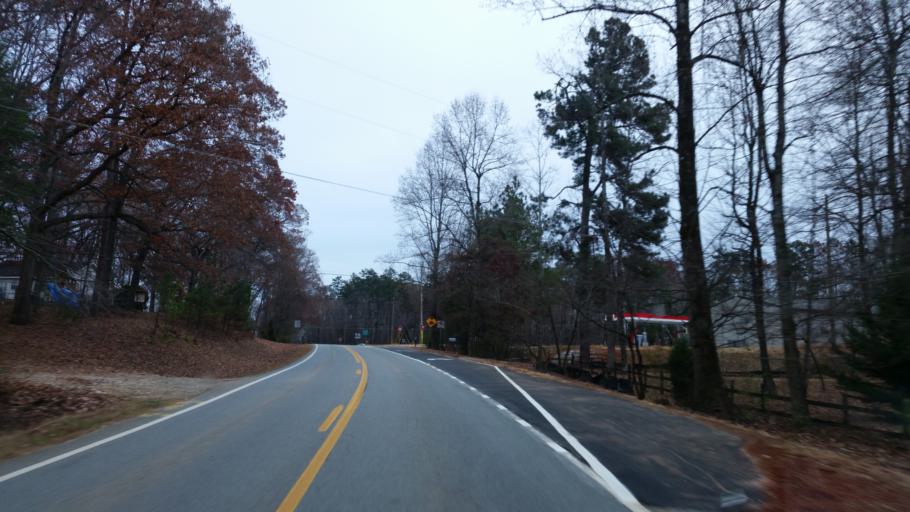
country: US
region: Georgia
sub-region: Dawson County
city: Dawsonville
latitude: 34.4424
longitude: -84.0960
